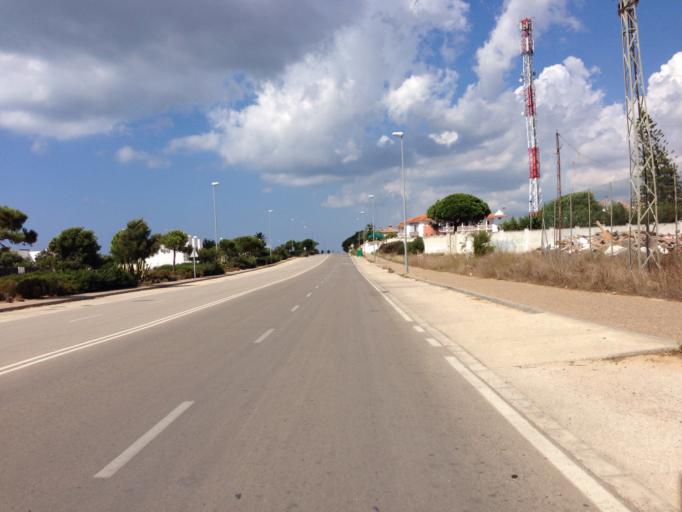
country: ES
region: Andalusia
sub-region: Provincia de Cadiz
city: Conil de la Frontera
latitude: 36.2856
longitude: -6.0956
